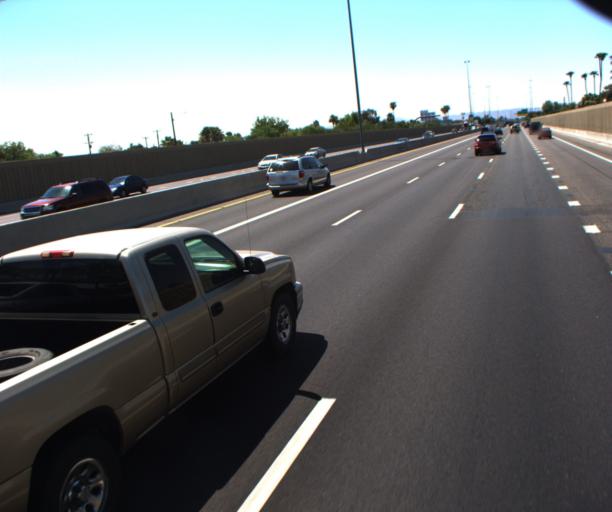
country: US
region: Arizona
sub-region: Maricopa County
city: Glendale
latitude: 33.5310
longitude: -112.1125
